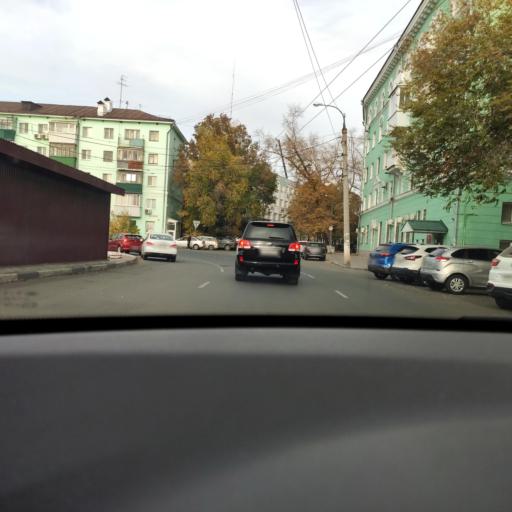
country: RU
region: Samara
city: Samara
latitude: 53.1946
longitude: 50.1267
